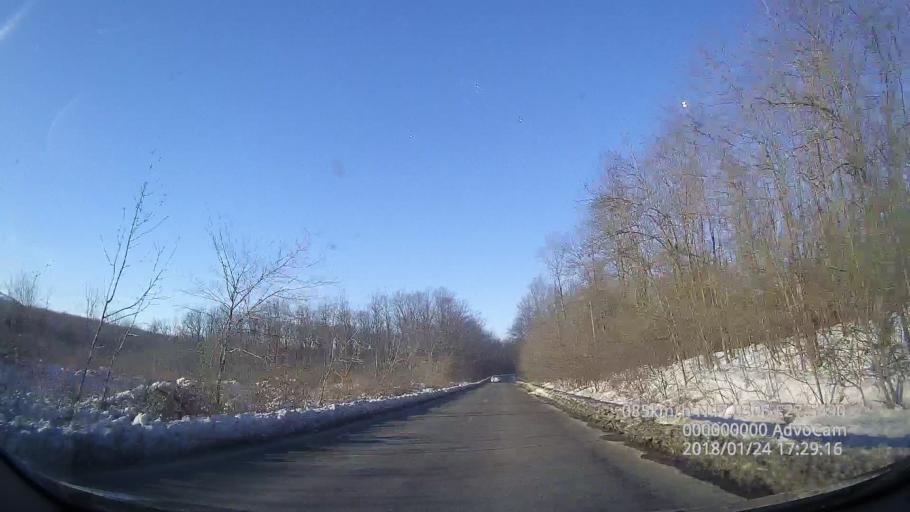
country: RO
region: Iasi
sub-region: Comuna Mogosesti
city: Mogosesti
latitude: 47.0312
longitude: 27.5486
